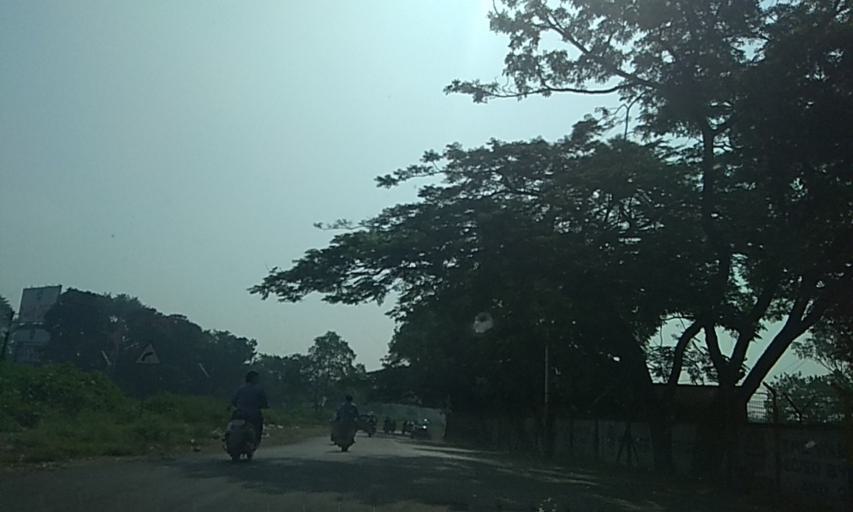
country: IN
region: Maharashtra
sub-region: Pune Division
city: Khadki
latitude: 18.5600
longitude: 73.8425
